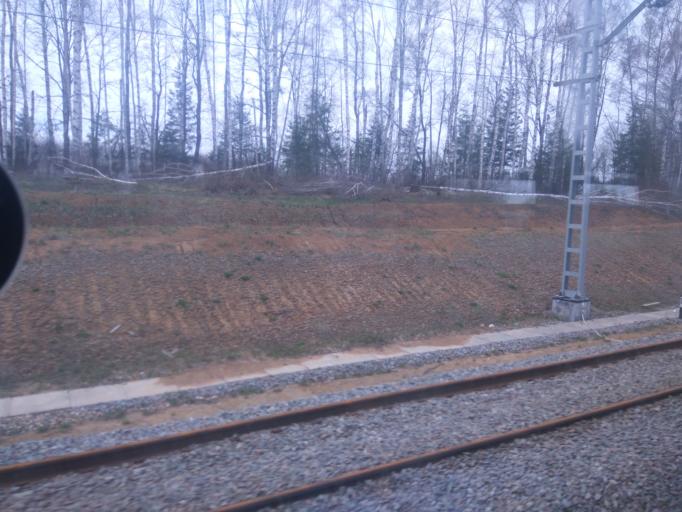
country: RU
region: Moskovskaya
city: Semkhoz
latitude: 56.3324
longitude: 38.0526
